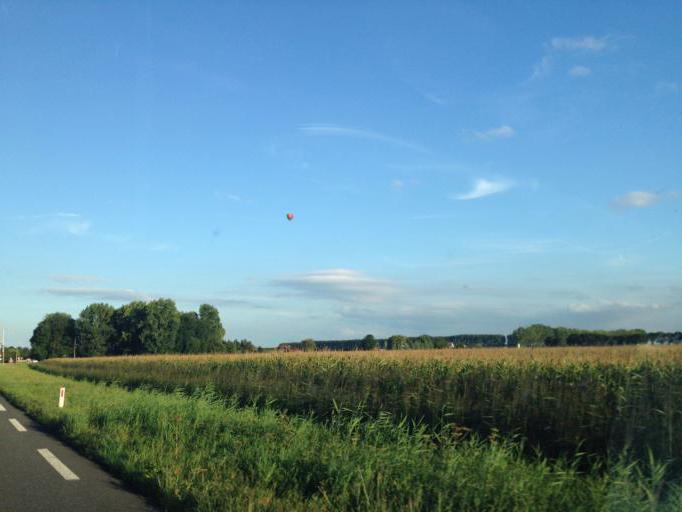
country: NL
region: South Holland
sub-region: Gemeente Leerdam
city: Leerdam
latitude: 51.8788
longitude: 5.1770
